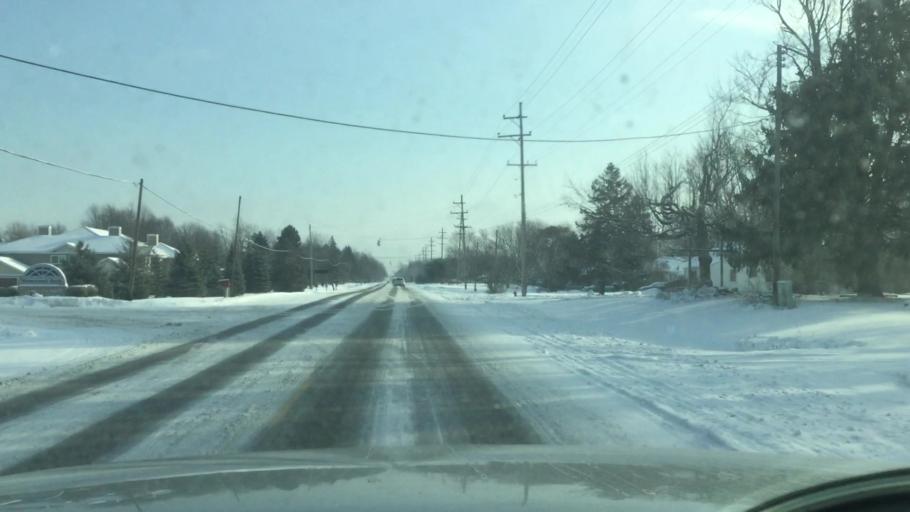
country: US
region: Michigan
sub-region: Genesee County
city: Mount Morris
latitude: 43.1047
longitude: -83.7069
